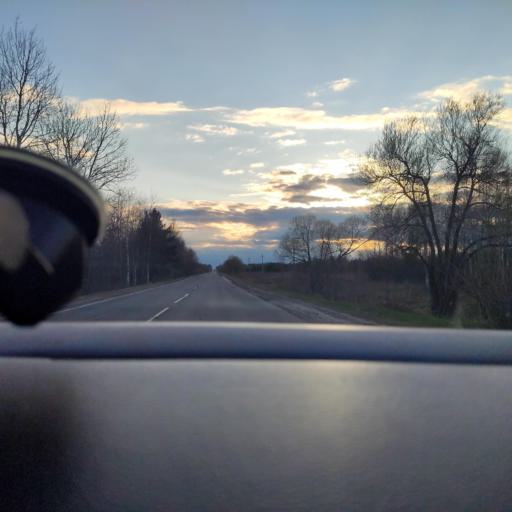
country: RU
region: Moskovskaya
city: Krasnyy Tkach
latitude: 55.4282
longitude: 39.2311
